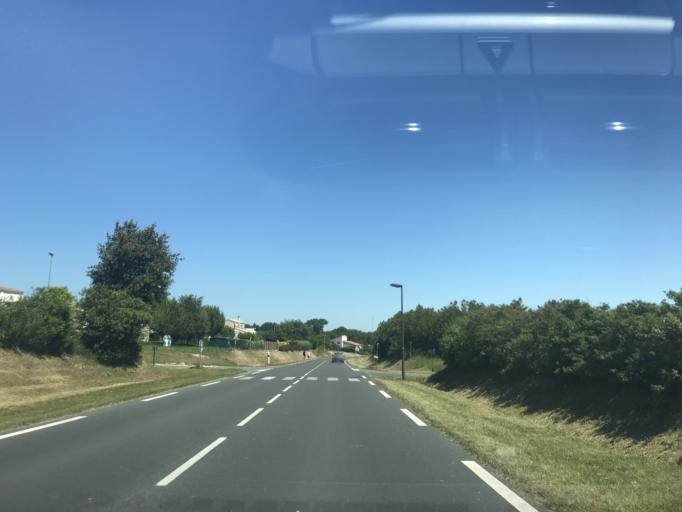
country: FR
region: Poitou-Charentes
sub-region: Departement de la Charente-Maritime
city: Meschers-sur-Gironde
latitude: 45.5651
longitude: -0.9574
